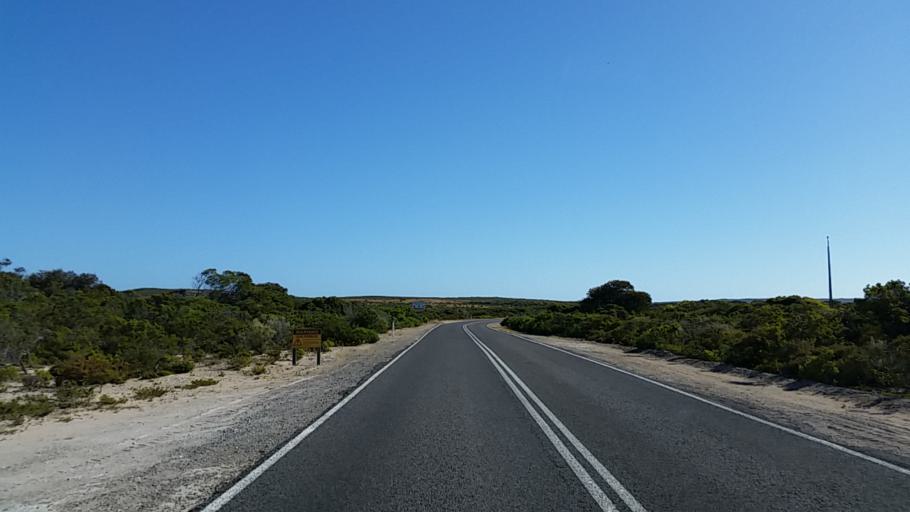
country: AU
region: South Australia
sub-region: Yorke Peninsula
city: Honiton
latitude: -35.2541
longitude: 136.9645
